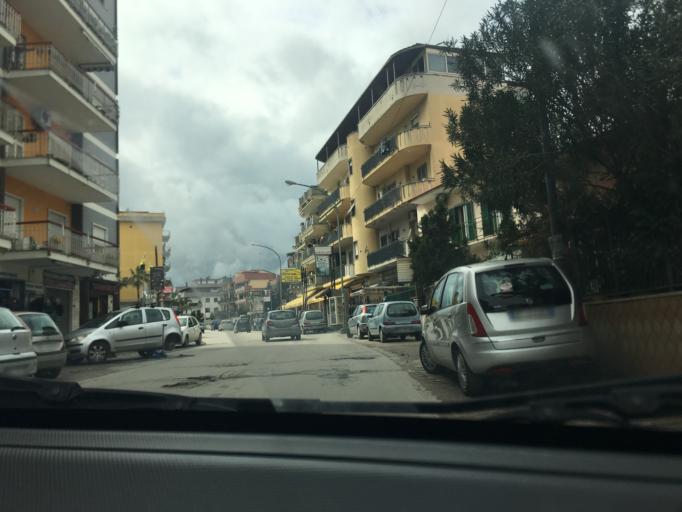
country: IT
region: Campania
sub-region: Provincia di Napoli
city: Marano di Napoli
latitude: 40.8959
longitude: 14.1827
